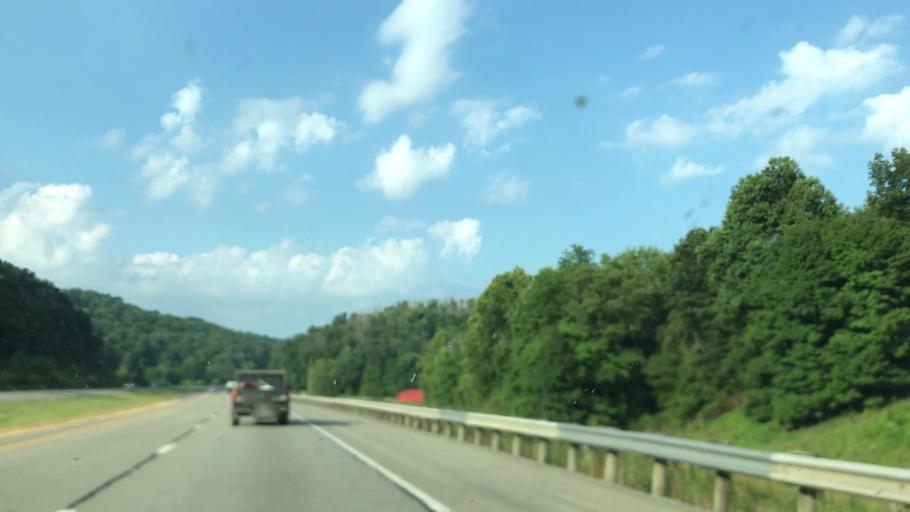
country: US
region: West Virginia
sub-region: Harrison County
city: Stonewood
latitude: 39.2056
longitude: -80.3109
